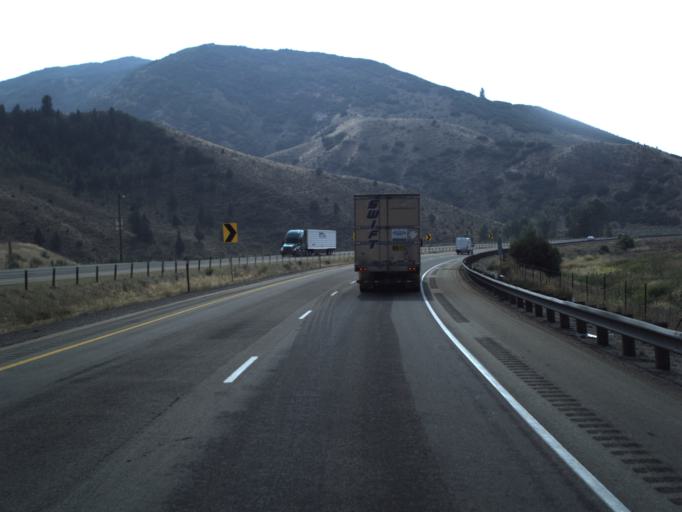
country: US
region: Utah
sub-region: Summit County
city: Coalville
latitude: 41.0133
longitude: -111.3692
